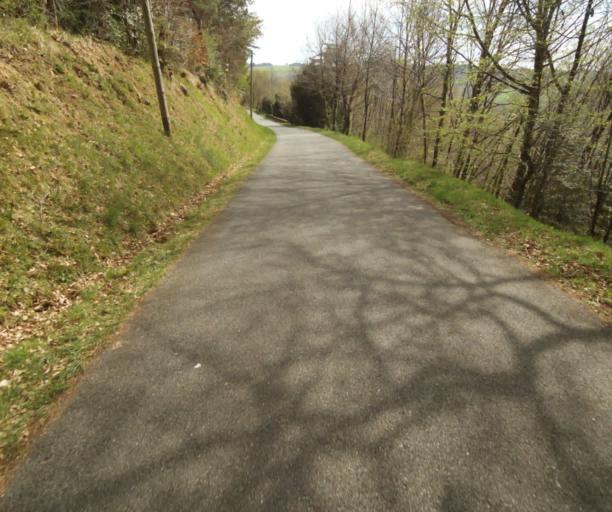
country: FR
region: Limousin
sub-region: Departement de la Correze
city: Naves
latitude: 45.3362
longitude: 1.8045
